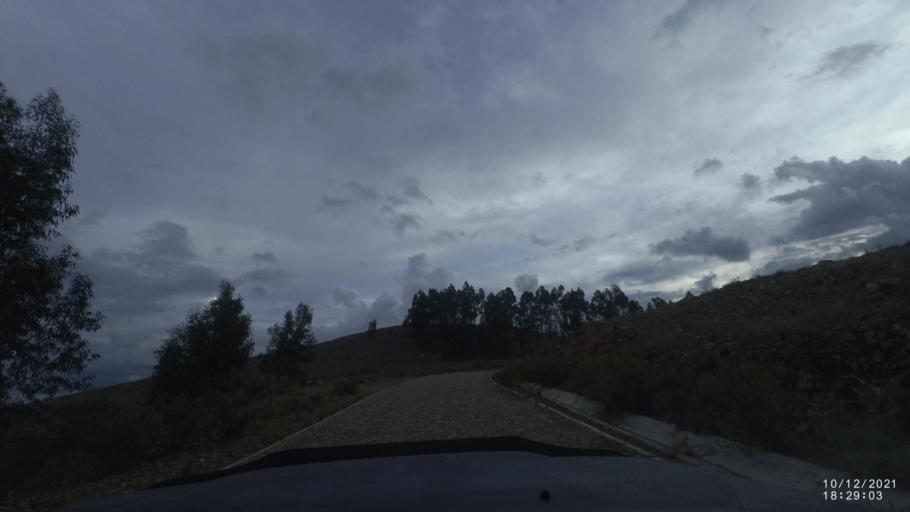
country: BO
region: Cochabamba
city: Tarata
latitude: -17.8122
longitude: -65.9748
